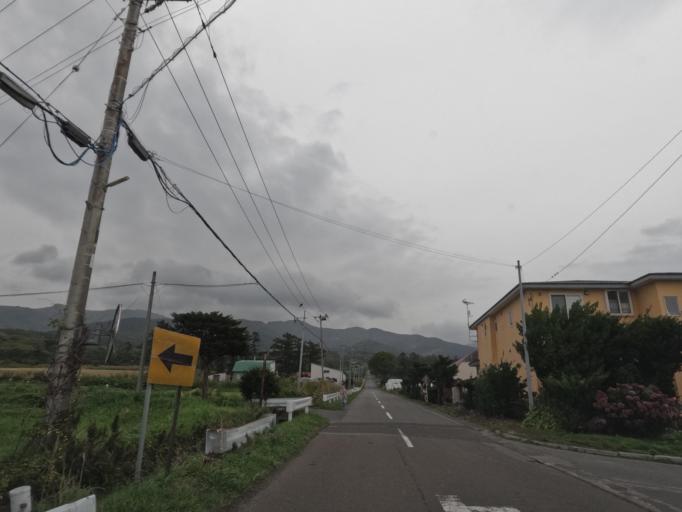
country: JP
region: Hokkaido
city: Date
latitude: 42.4740
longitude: 140.8951
